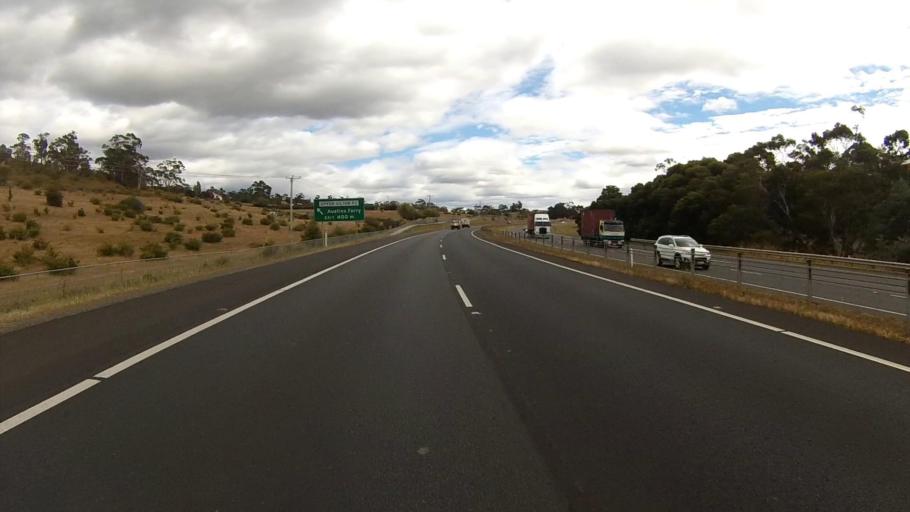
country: AU
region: Tasmania
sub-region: Glenorchy
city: Claremont
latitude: -42.7822
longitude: 147.2391
